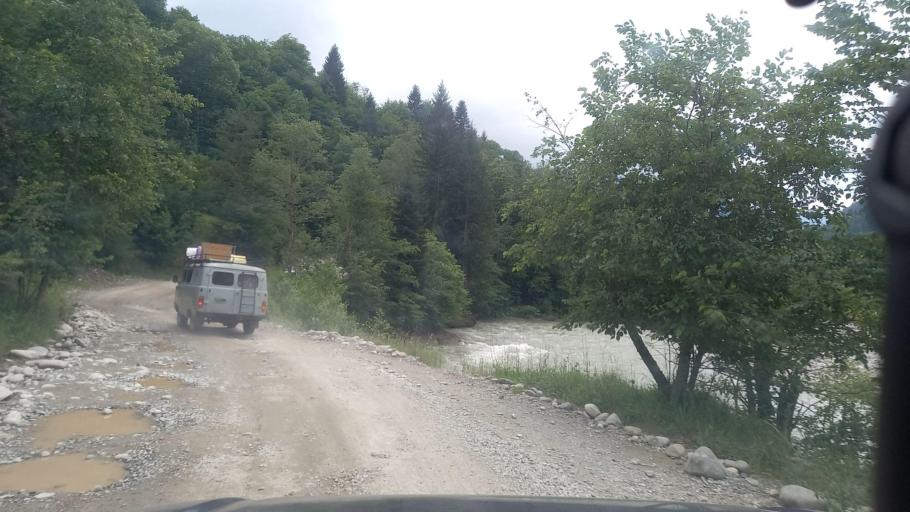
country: RU
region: Karachayevo-Cherkesiya
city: Kurdzhinovo
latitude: 43.8187
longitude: 40.9149
